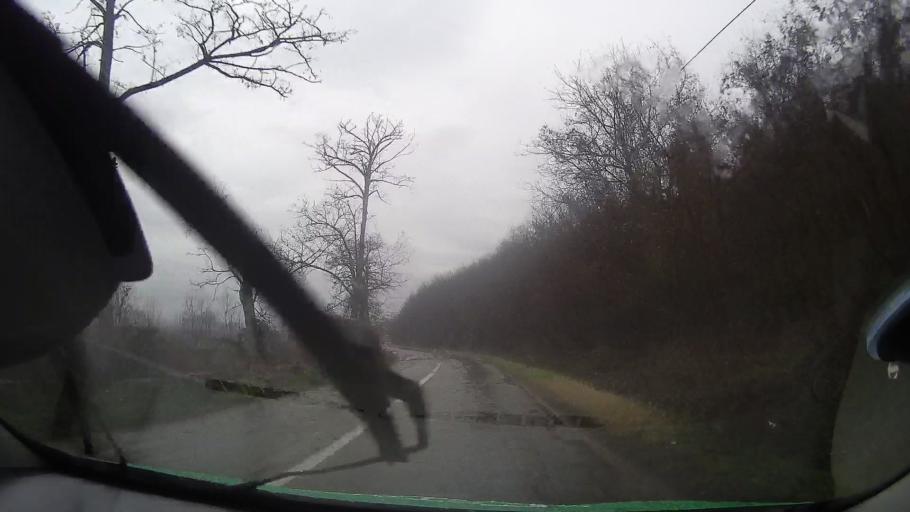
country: RO
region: Bihor
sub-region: Comuna Holod
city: Holod
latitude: 46.7754
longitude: 22.1361
